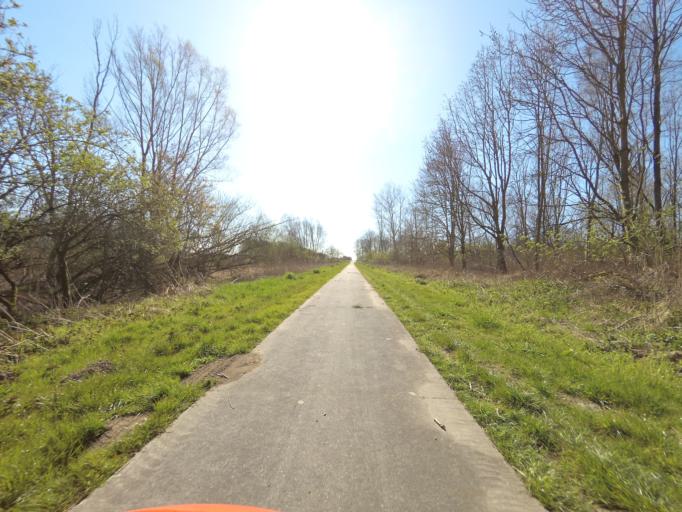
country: NL
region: Flevoland
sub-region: Gemeente Lelystad
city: Lelystad
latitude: 52.4261
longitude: 5.4195
